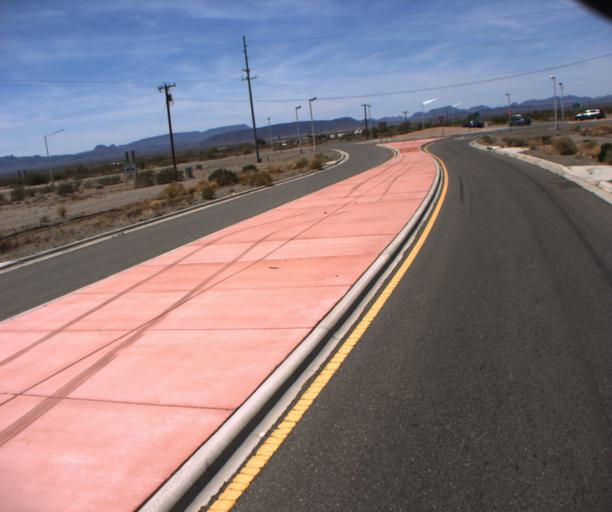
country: US
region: Arizona
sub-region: La Paz County
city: Salome
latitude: 33.7186
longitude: -113.7662
